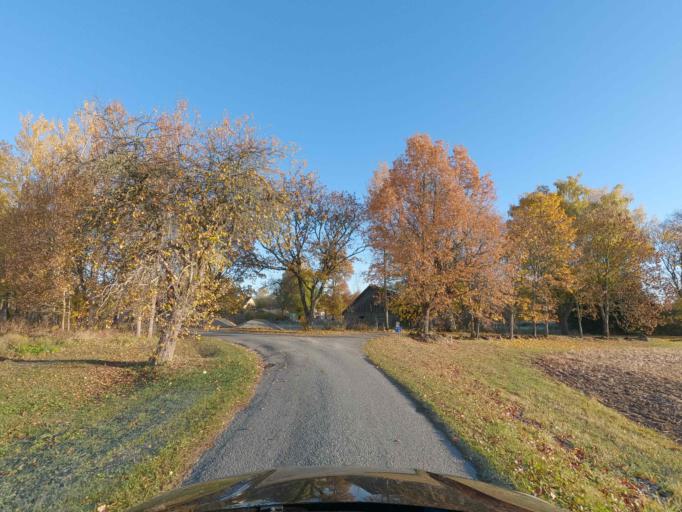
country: EE
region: Raplamaa
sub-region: Rapla vald
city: Rapla
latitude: 59.0562
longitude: 24.8594
